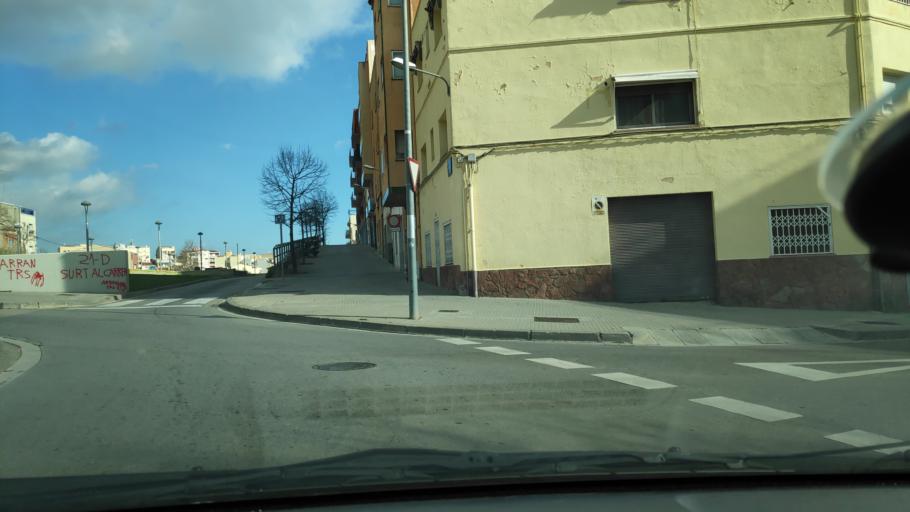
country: ES
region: Catalonia
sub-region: Provincia de Barcelona
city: Terrassa
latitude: 41.5659
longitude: 1.9969
